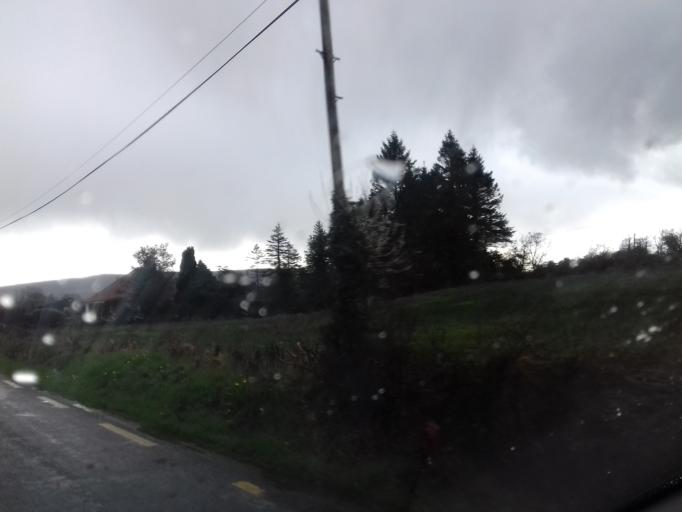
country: IE
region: Connaught
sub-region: County Leitrim
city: Manorhamilton
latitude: 54.2725
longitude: -7.9379
